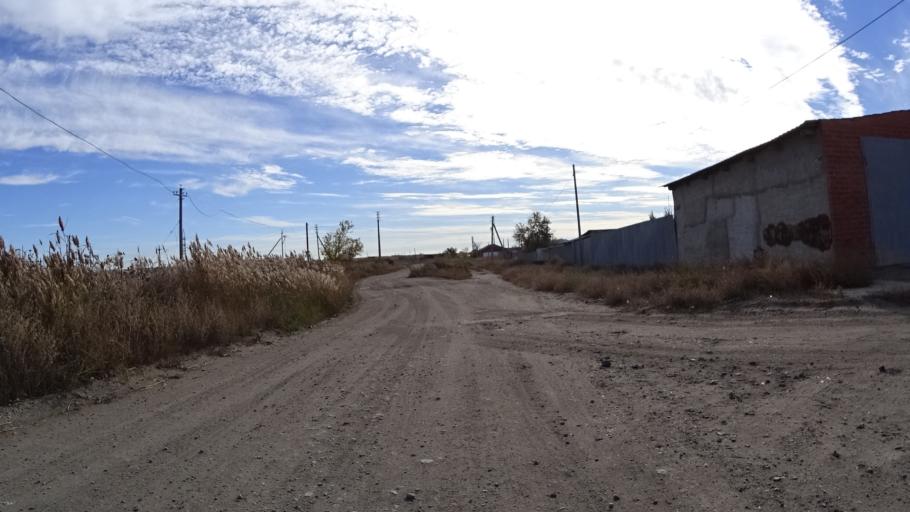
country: RU
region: Chelyabinsk
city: Troitsk
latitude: 54.0752
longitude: 61.5895
